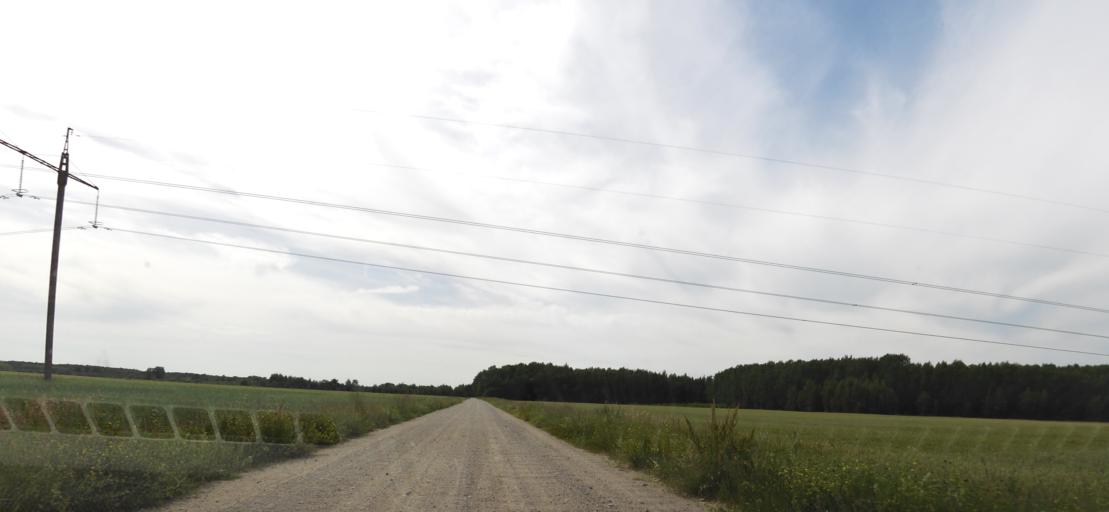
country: LT
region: Panevezys
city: Pasvalys
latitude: 55.9660
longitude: 24.3155
